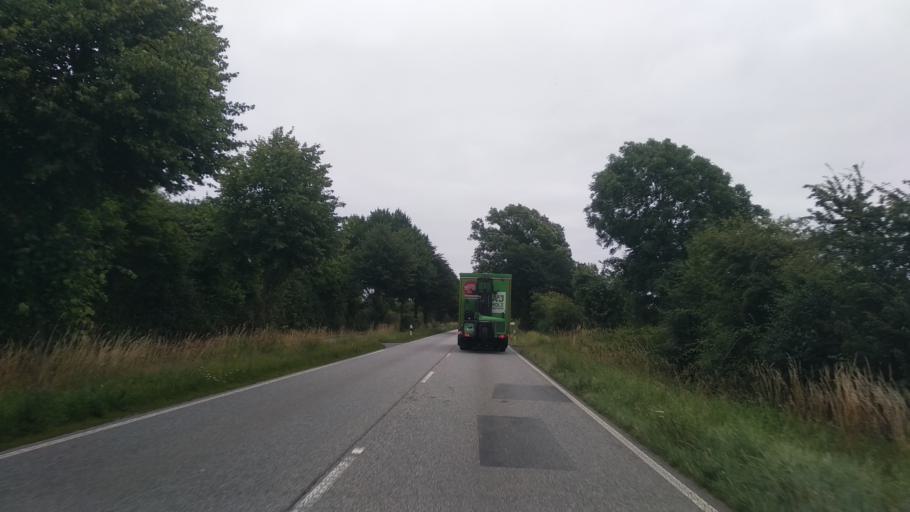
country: DE
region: Schleswig-Holstein
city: Wees
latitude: 54.8044
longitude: 9.5176
